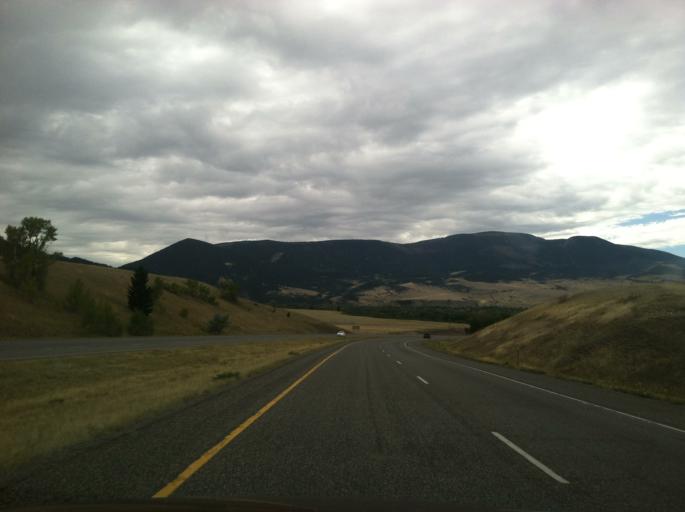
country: US
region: Montana
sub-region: Park County
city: Livingston
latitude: 45.6464
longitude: -110.5505
